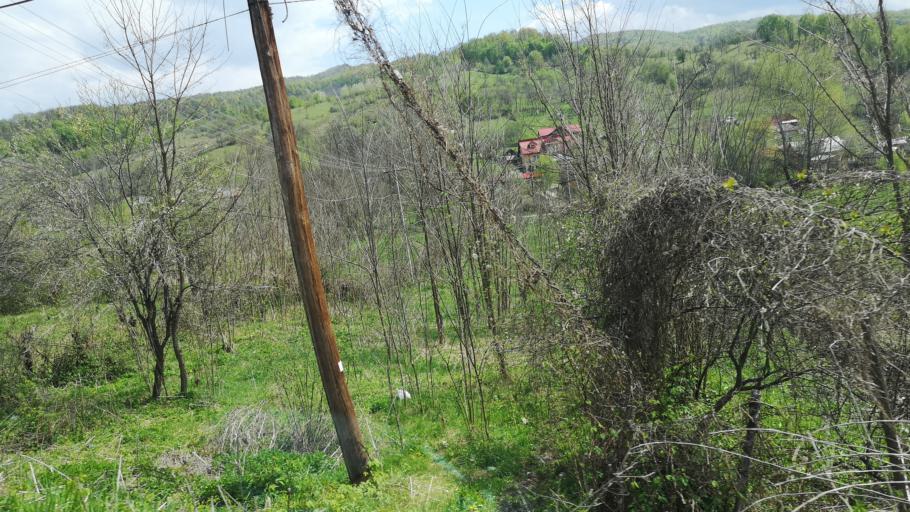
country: RO
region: Prahova
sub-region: Comuna Soimari
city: Soimari
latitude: 45.1576
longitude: 26.2044
